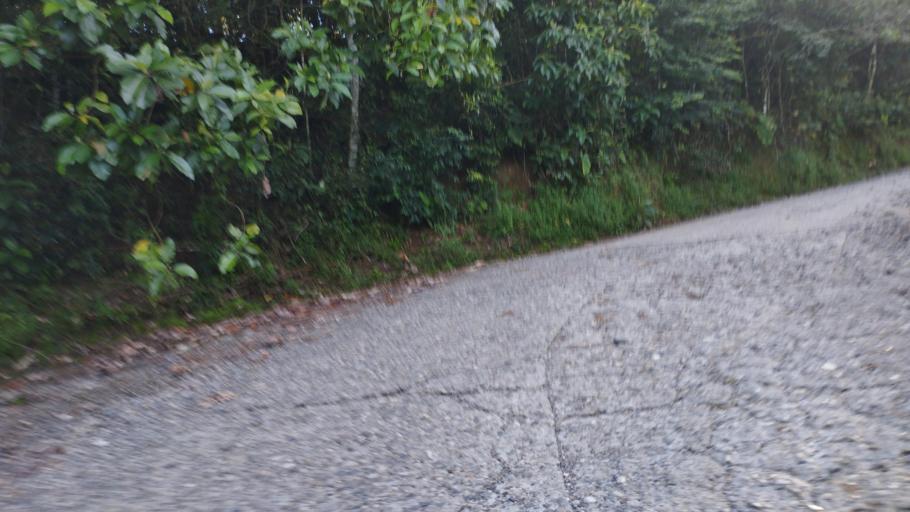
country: CO
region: Casanare
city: Sabanalarga
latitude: 4.8140
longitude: -73.0919
